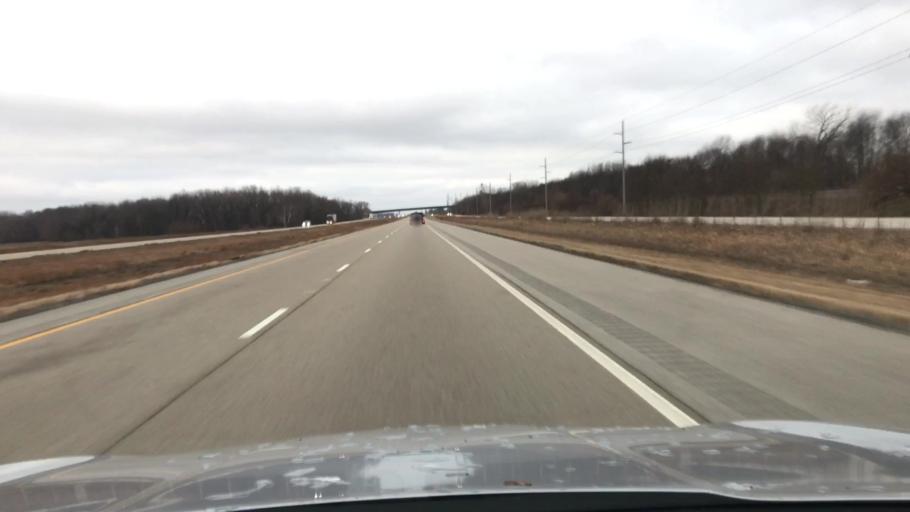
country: US
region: Illinois
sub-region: Logan County
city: Atlanta
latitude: 40.2274
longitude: -89.2706
